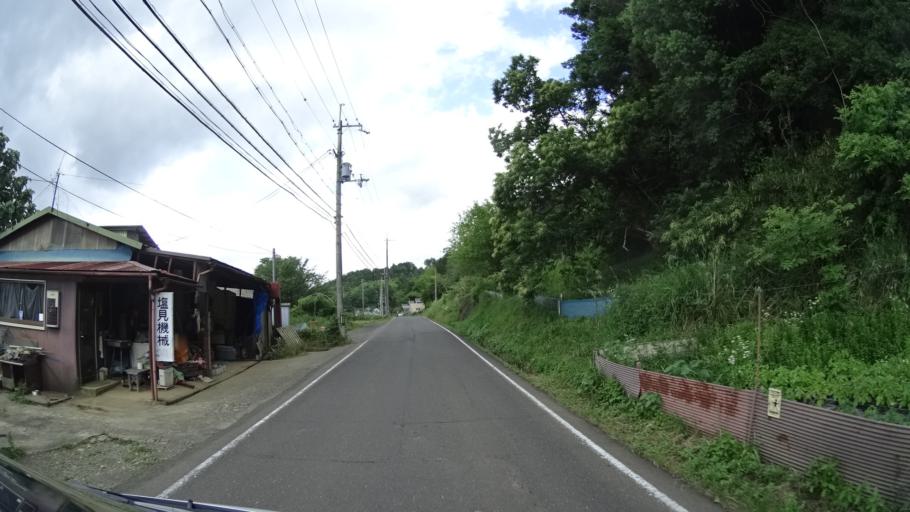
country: JP
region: Kyoto
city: Ayabe
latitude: 35.3347
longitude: 135.2040
